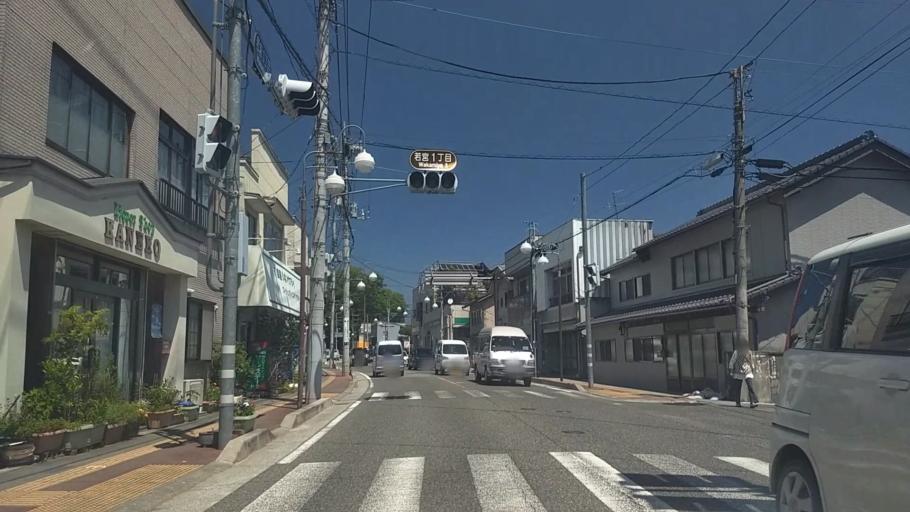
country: JP
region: Yamanashi
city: Nirasaki
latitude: 35.7124
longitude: 138.4492
